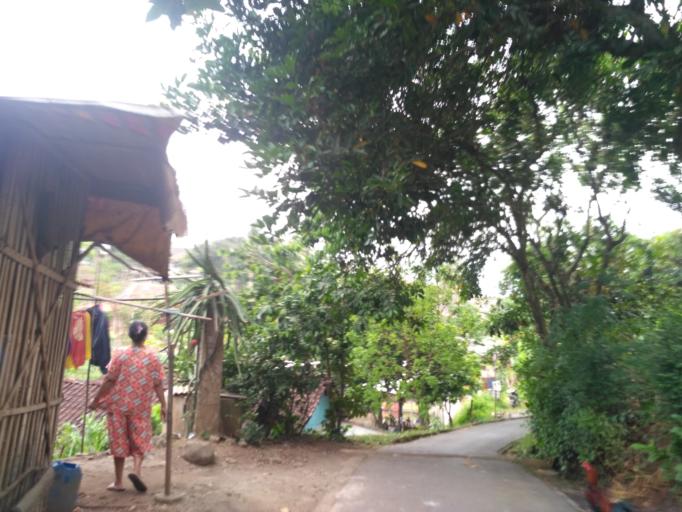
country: ID
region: Central Java
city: Ungaran
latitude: -7.0761
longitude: 110.4221
